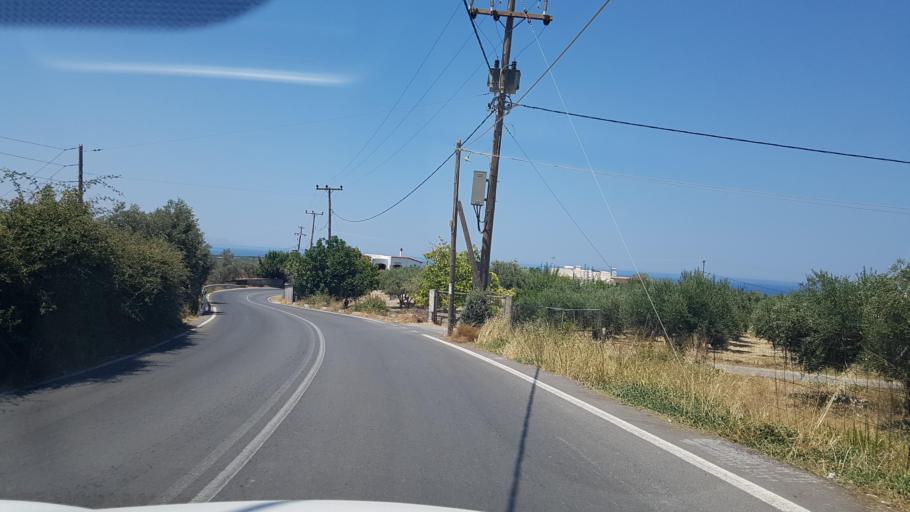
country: GR
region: Crete
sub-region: Nomos Rethymnis
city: Agia Foteini
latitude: 35.3532
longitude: 24.5889
